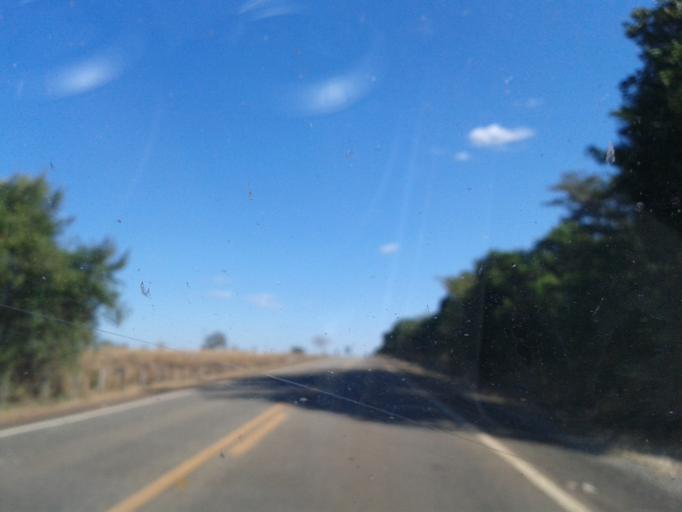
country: BR
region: Goias
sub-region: Mozarlandia
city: Mozarlandia
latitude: -14.3152
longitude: -50.4076
